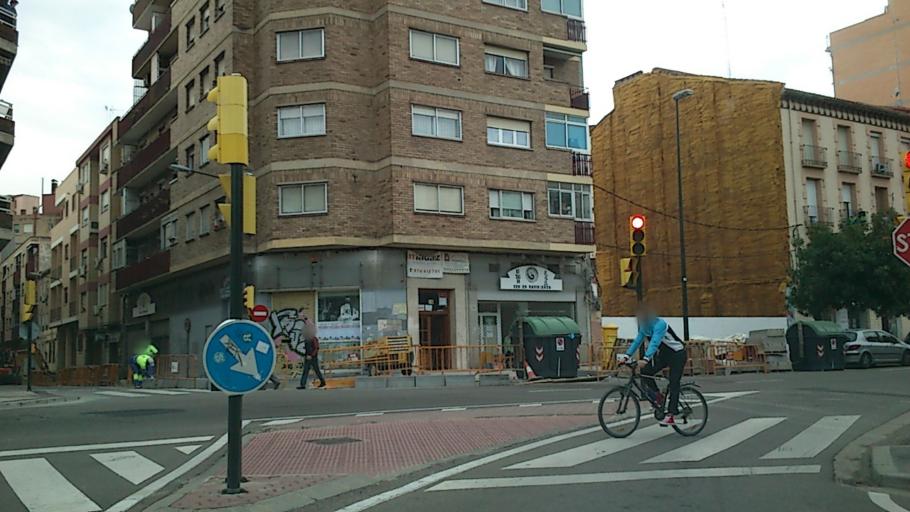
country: ES
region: Aragon
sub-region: Provincia de Zaragoza
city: Zaragoza
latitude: 41.6593
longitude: -0.8719
